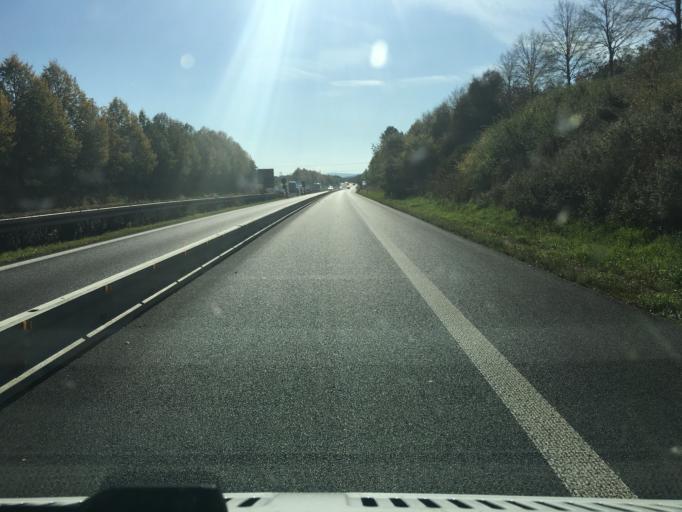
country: DE
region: Saxony
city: Zwickau
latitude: 50.7592
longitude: 12.5023
